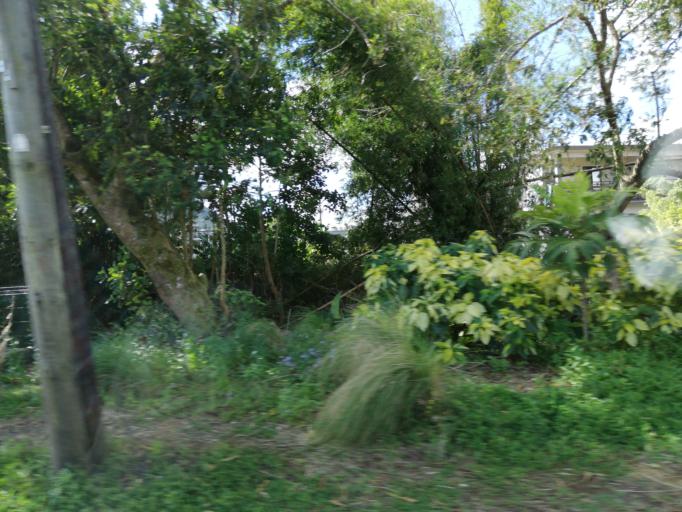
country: MU
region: Pamplemousses
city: Creve Coeur
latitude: -20.2022
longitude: 57.5590
